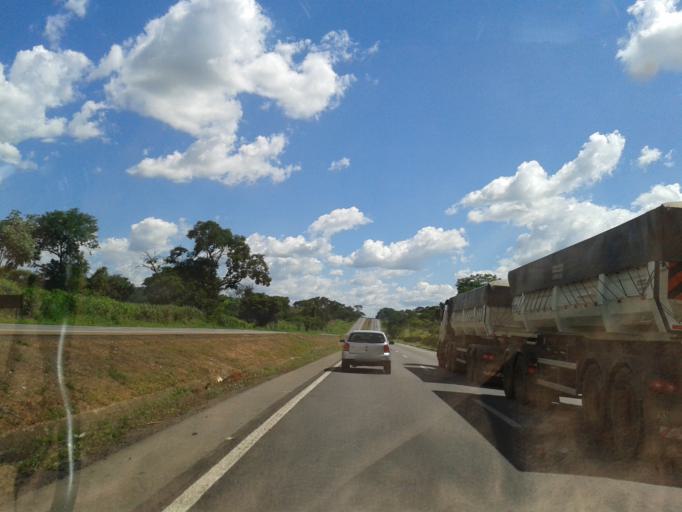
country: BR
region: Goias
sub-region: Piracanjuba
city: Piracanjuba
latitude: -17.4140
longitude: -49.2259
